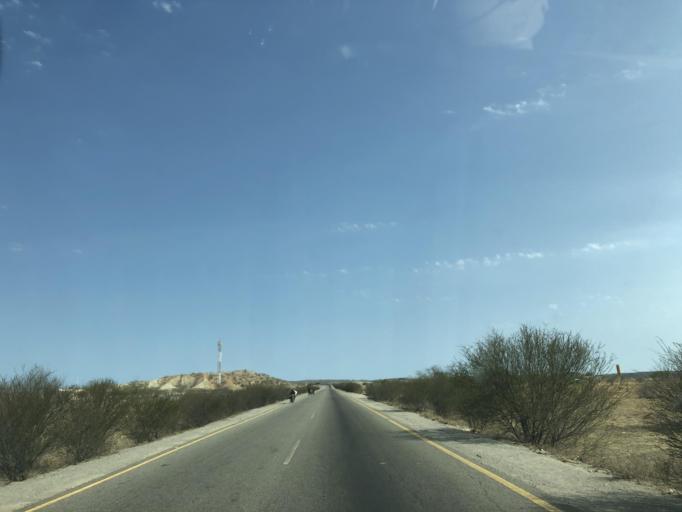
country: AO
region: Benguela
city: Benguela
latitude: -12.7407
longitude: 13.3517
